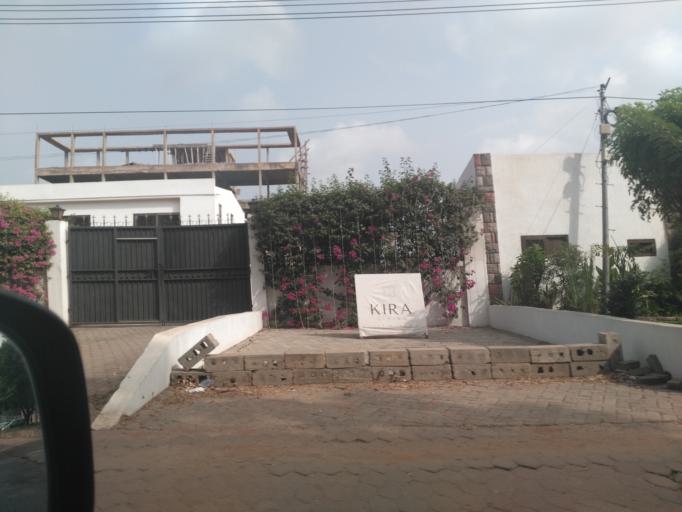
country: GH
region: Greater Accra
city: Accra
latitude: 5.6095
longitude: -0.1800
